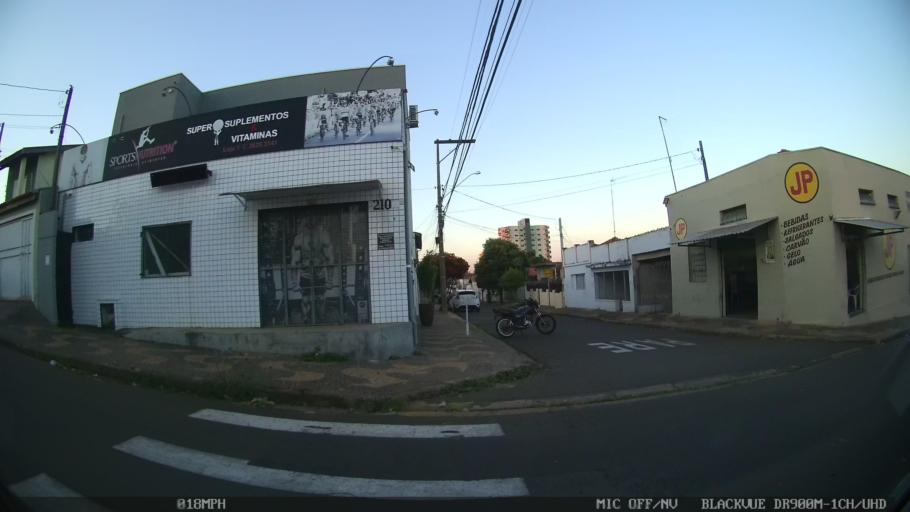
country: BR
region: Sao Paulo
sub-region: Santa Barbara D'Oeste
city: Santa Barbara d'Oeste
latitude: -22.7597
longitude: -47.4137
